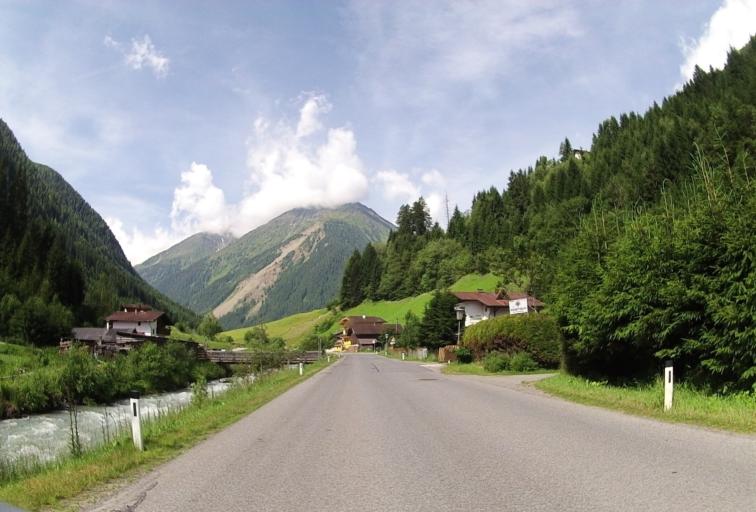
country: AT
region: Tyrol
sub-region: Politischer Bezirk Innsbruck Land
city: Gries im Sellrain
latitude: 47.2020
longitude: 11.1762
